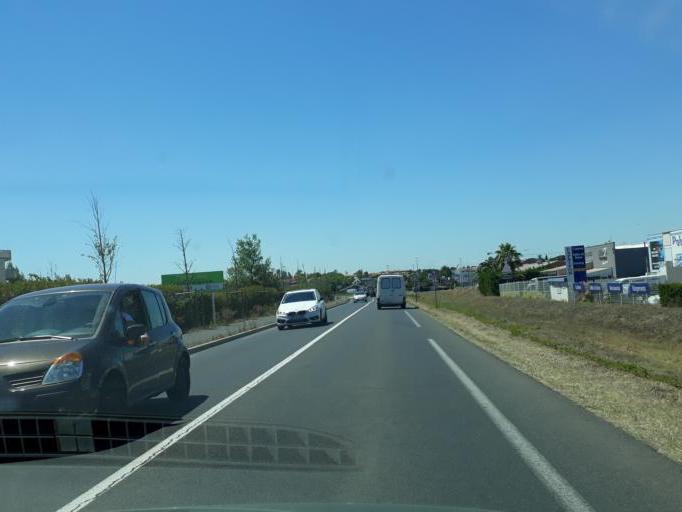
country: FR
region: Languedoc-Roussillon
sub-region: Departement de l'Herault
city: Agde
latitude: 43.3077
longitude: 3.4978
